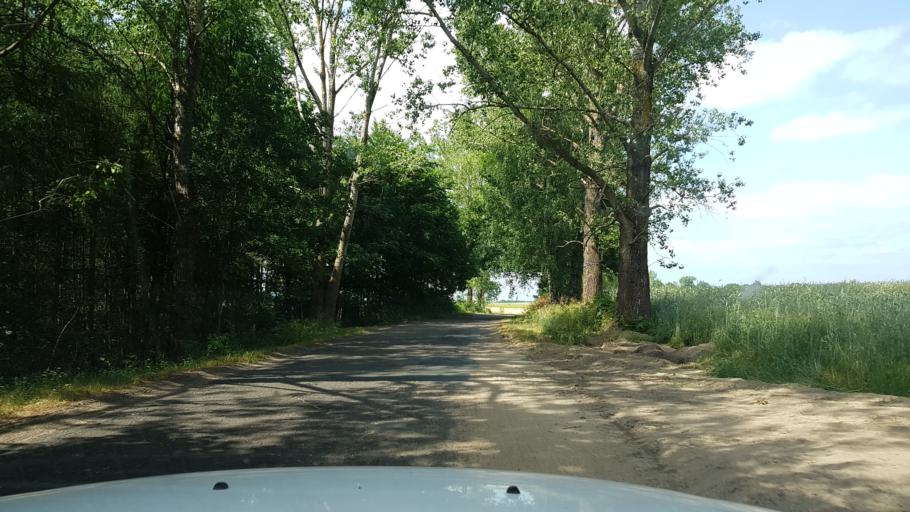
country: PL
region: West Pomeranian Voivodeship
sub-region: Powiat goleniowski
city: Mosty
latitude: 53.5685
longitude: 14.9741
